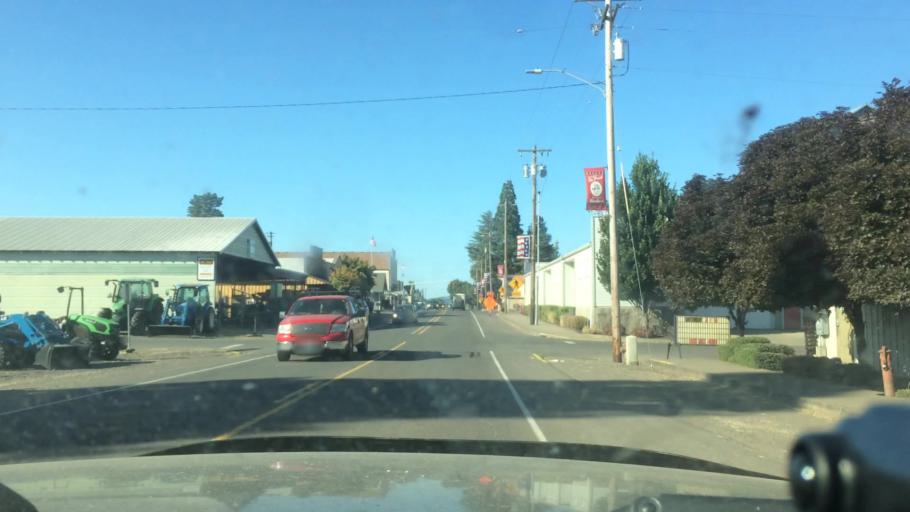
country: US
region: Oregon
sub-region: Yamhill County
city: Dundee
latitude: 45.2094
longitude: -122.9778
